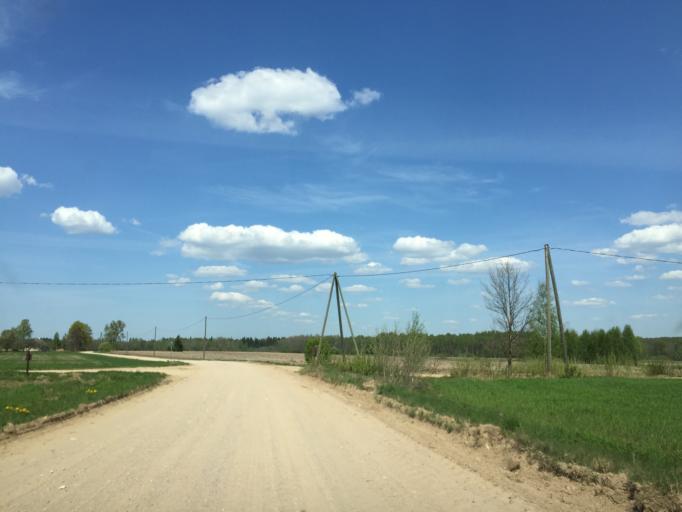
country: LV
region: Limbazu Rajons
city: Limbazi
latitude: 57.3509
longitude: 24.6504
